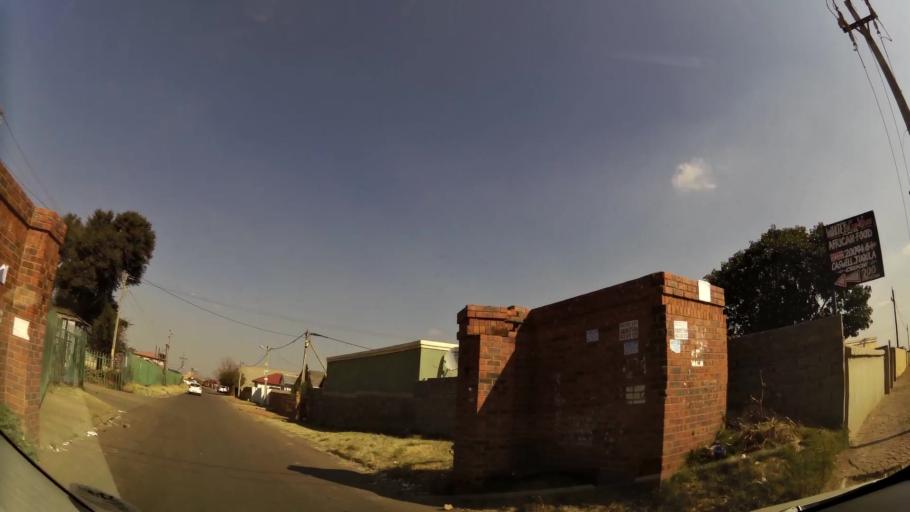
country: ZA
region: Gauteng
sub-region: City of Johannesburg Metropolitan Municipality
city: Roodepoort
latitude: -26.1644
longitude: 27.7972
